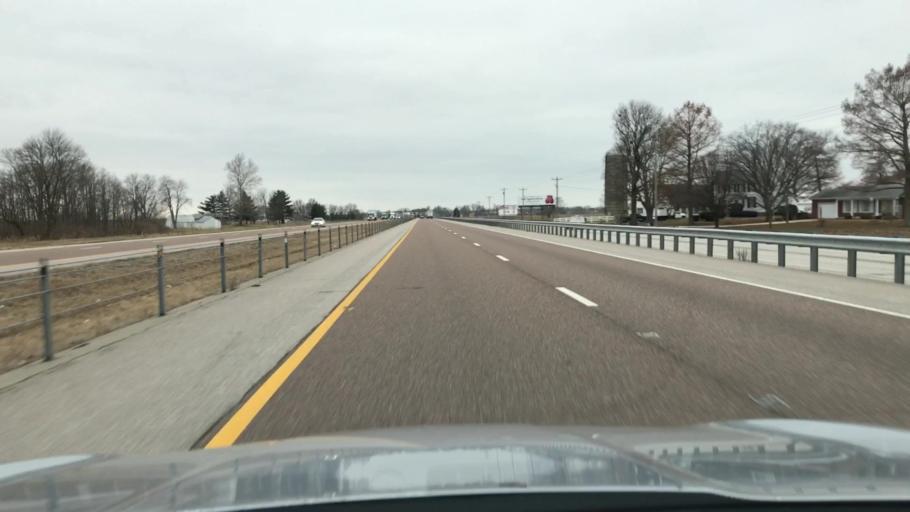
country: US
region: Illinois
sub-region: Madison County
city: Worden
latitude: 38.9090
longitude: -89.8233
